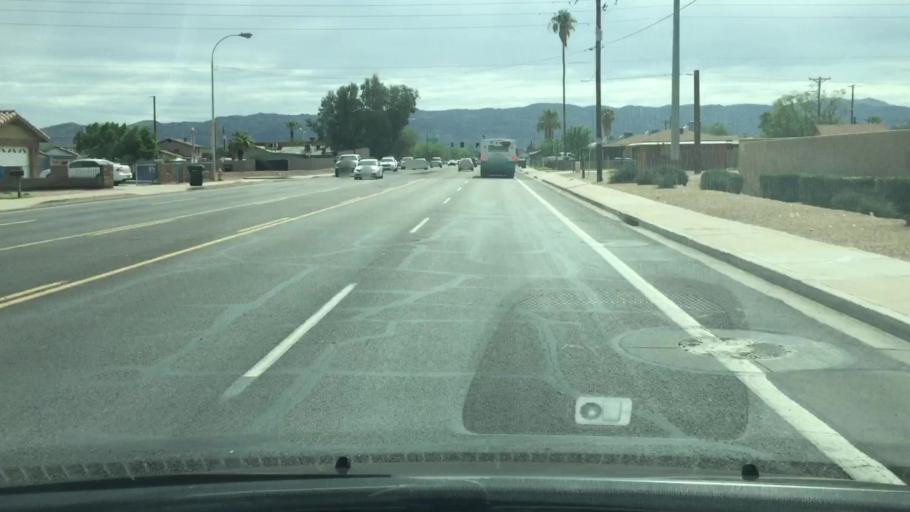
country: US
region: Arizona
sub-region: Maricopa County
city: Phoenix
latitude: 33.4093
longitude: -112.0299
